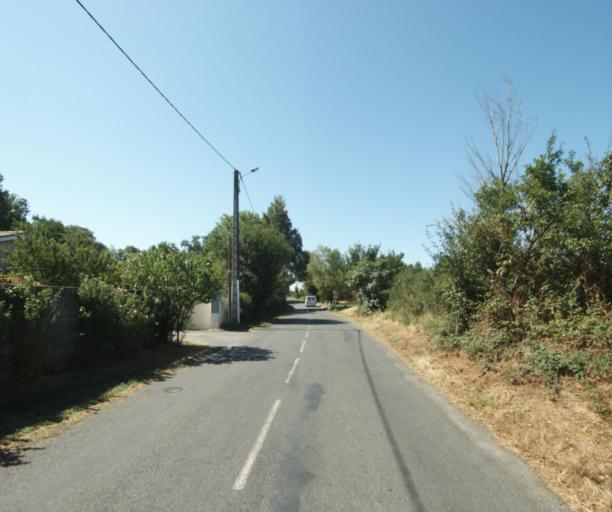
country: FR
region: Midi-Pyrenees
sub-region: Departement de la Haute-Garonne
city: Revel
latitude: 43.4672
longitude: 1.9908
